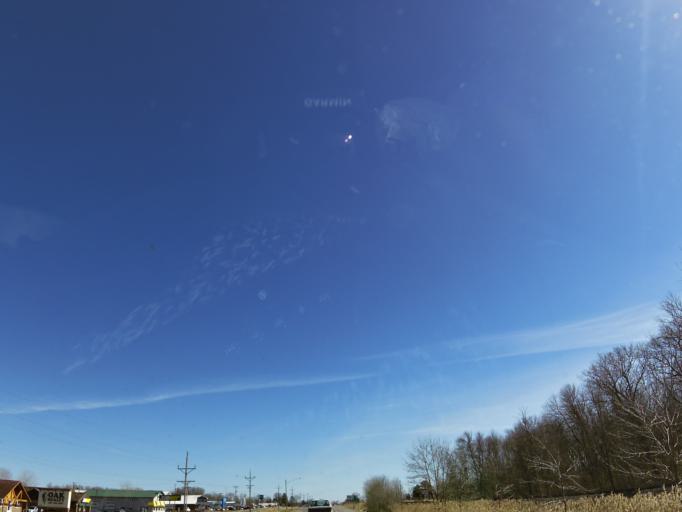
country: US
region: Minnesota
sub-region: Wright County
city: Annandale
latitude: 45.2573
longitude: -94.1132
